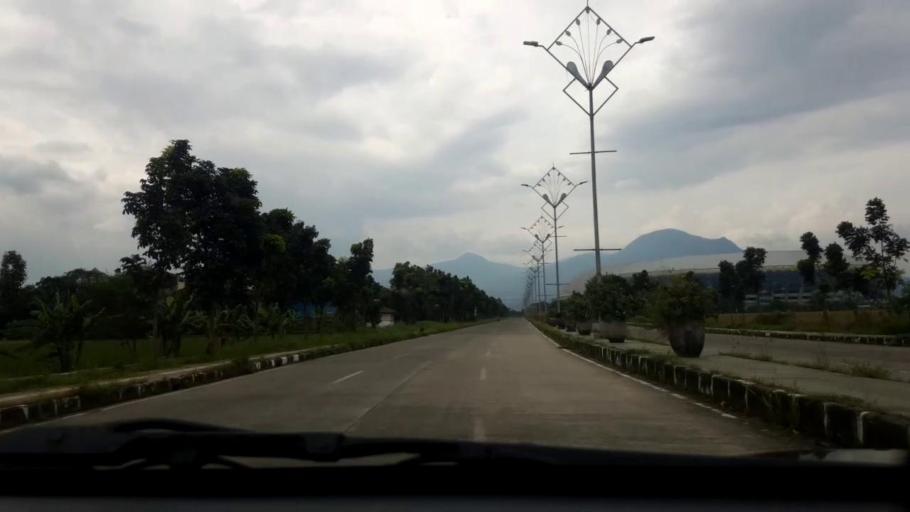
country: ID
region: West Java
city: Cileunyi
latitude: -6.9629
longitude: 107.7096
